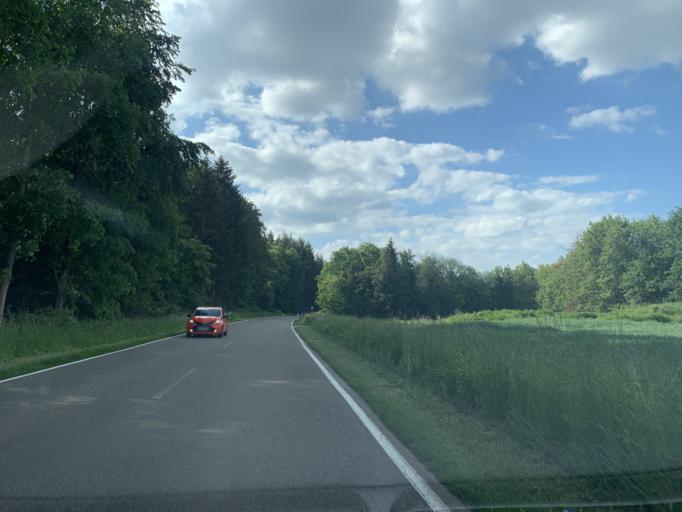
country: DE
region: Baden-Wuerttemberg
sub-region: Tuebingen Region
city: Huttisheim
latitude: 48.3174
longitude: 9.9377
